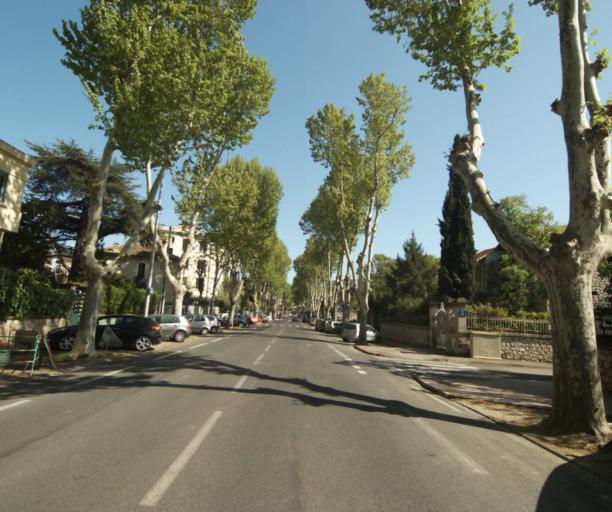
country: FR
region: Languedoc-Roussillon
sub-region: Departement de l'Herault
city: Montpellier
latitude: 43.6148
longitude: 3.8645
